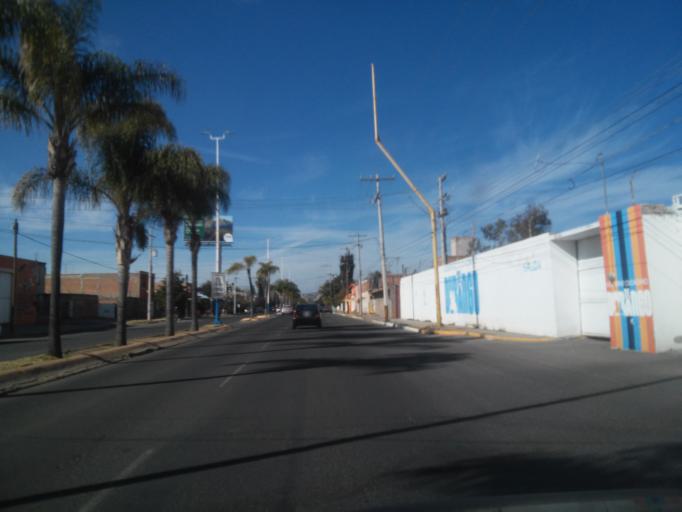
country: MX
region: Durango
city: Victoria de Durango
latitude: 24.0396
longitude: -104.6597
